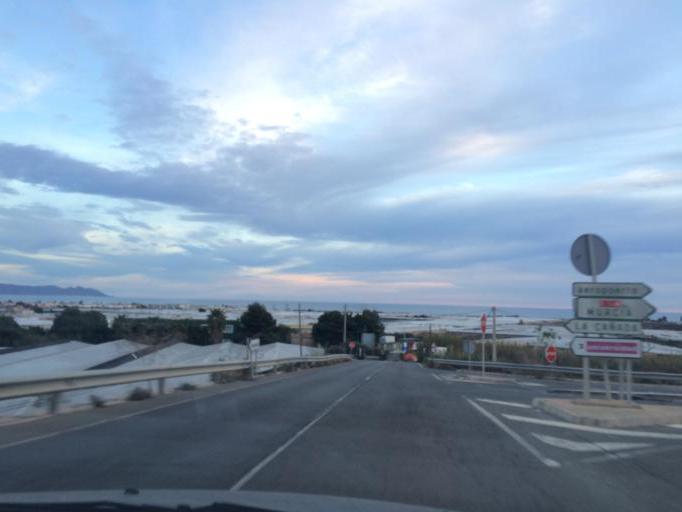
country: ES
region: Andalusia
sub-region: Provincia de Almeria
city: Viator
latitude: 36.8435
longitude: -2.3989
